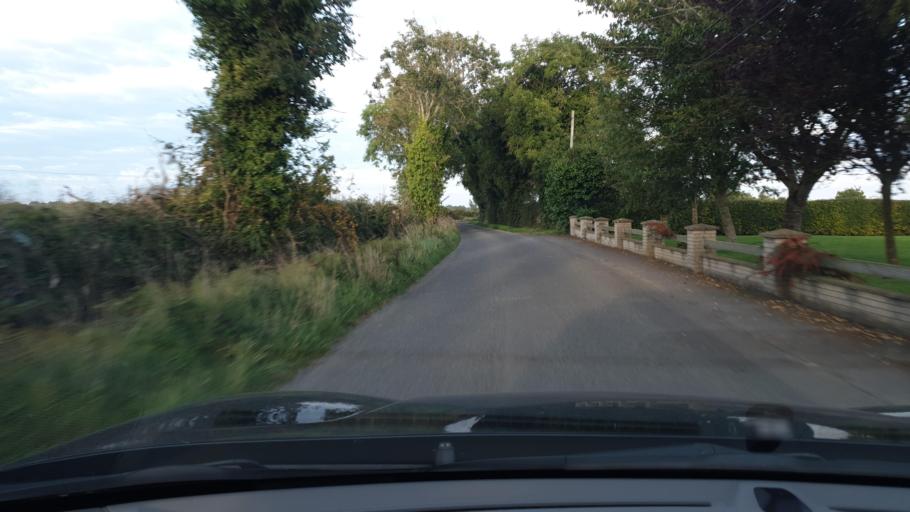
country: IE
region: Leinster
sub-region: An Mhi
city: Ashbourne
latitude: 53.5254
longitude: -6.3763
